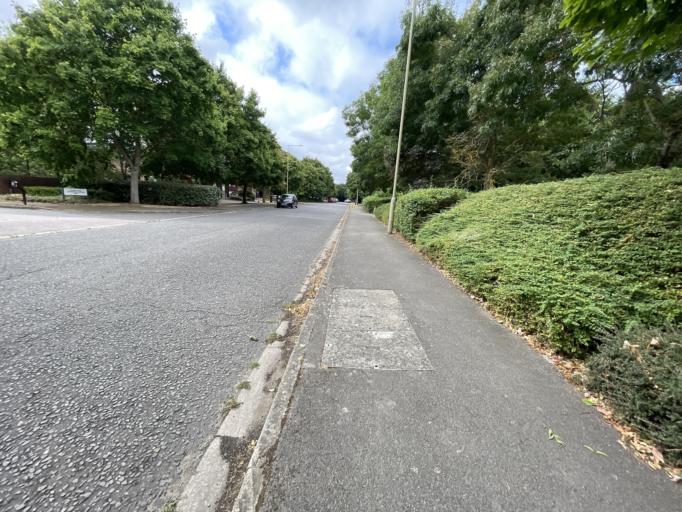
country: GB
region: England
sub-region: Oxfordshire
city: Abingdon
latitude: 51.6727
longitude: -1.2648
